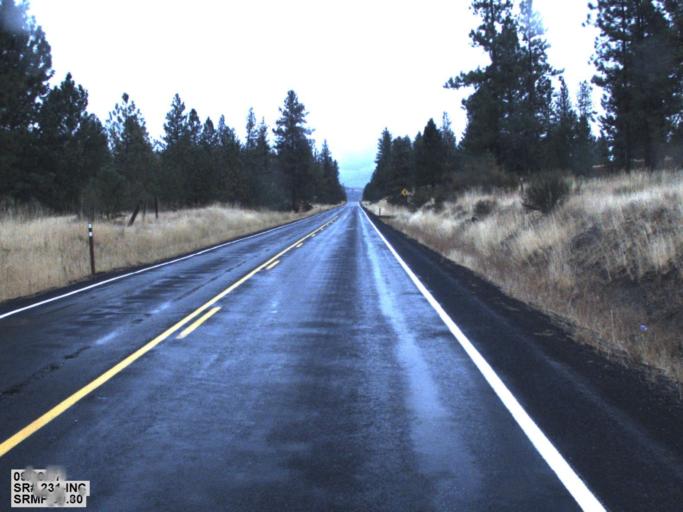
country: US
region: Washington
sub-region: Lincoln County
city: Davenport
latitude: 47.7863
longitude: -117.8895
